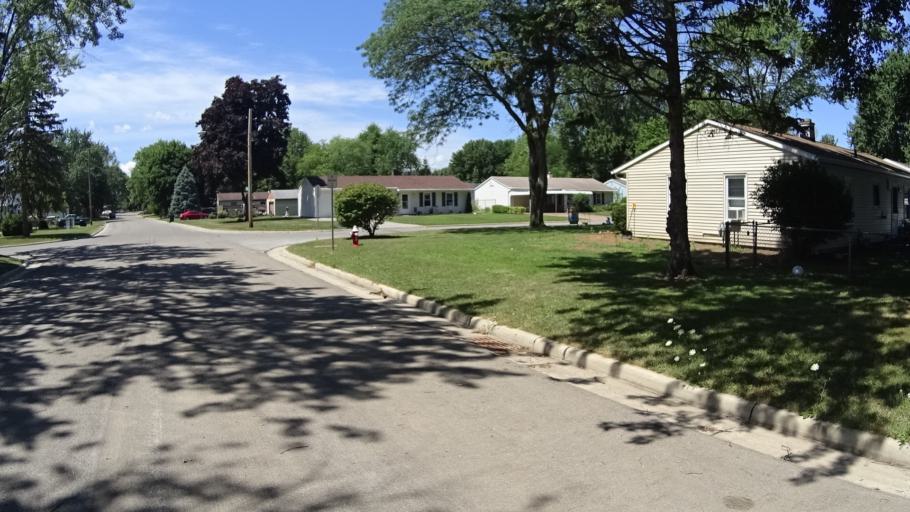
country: US
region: Ohio
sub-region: Erie County
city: Sandusky
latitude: 41.4017
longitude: -82.6728
